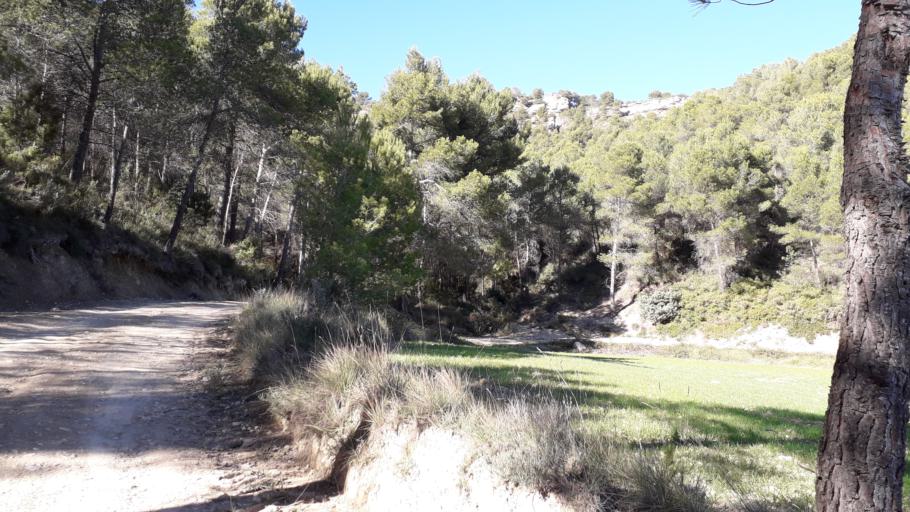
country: ES
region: Catalonia
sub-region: Provincia de Barcelona
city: Sant Marti de Tous
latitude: 41.5231
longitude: 1.5146
